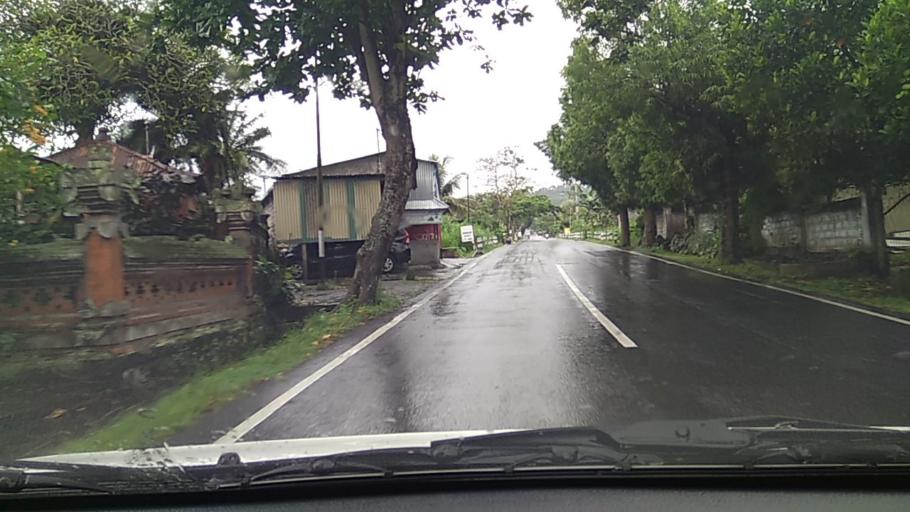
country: ID
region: Bali
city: Banjar Ababi
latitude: -8.4197
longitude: 115.5917
